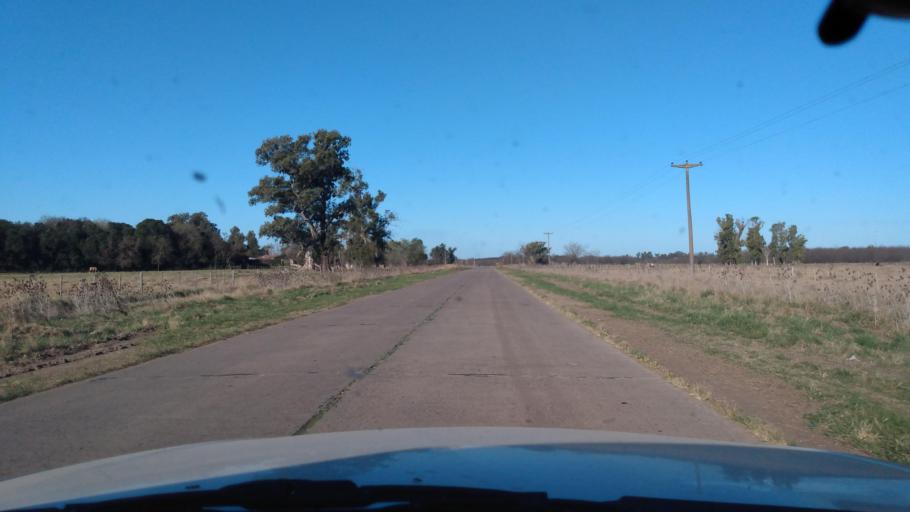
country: AR
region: Buenos Aires
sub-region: Partido de Mercedes
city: Mercedes
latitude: -34.6140
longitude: -59.2723
